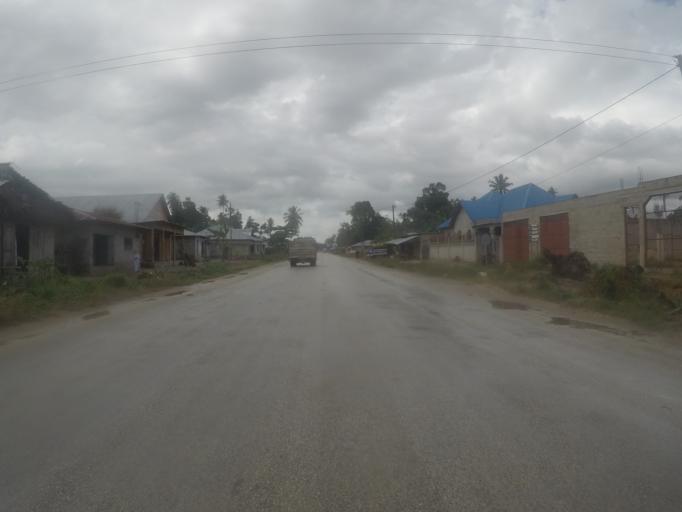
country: TZ
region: Zanzibar Central/South
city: Koani
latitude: -6.0211
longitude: 39.2419
